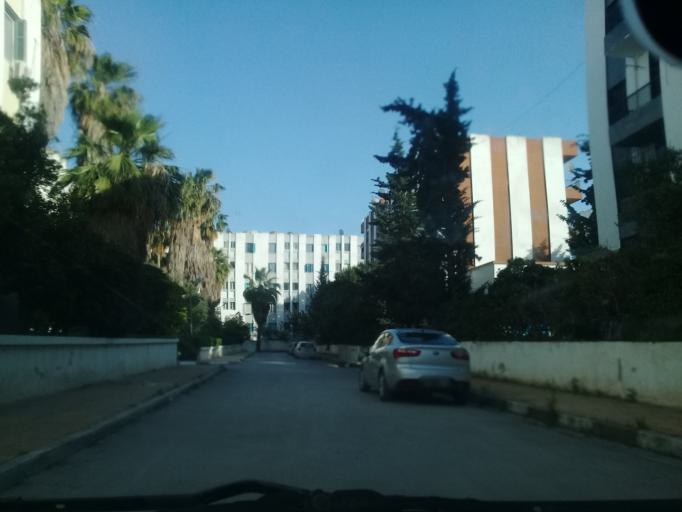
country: TN
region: Ariana
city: Ariana
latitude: 36.8370
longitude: 10.1992
